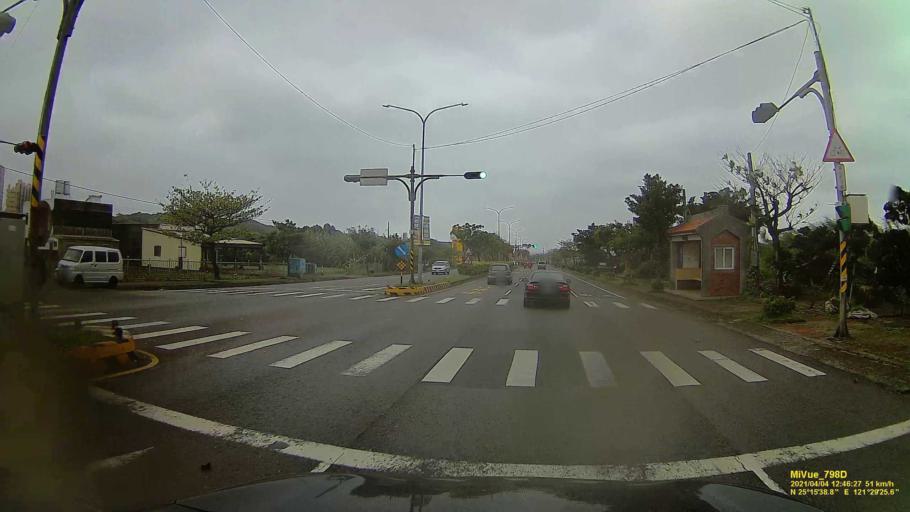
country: TW
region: Taipei
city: Taipei
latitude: 25.2609
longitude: 121.4902
